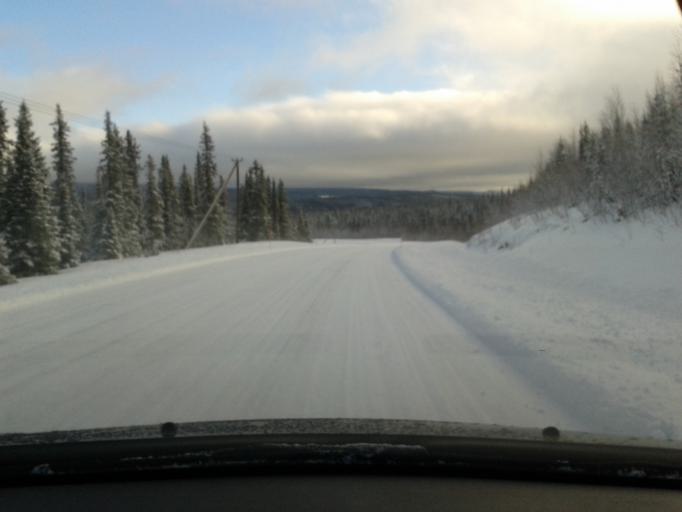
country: SE
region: Vaesterbotten
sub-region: Vilhelmina Kommun
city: Sjoberg
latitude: 65.2570
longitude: 15.6649
